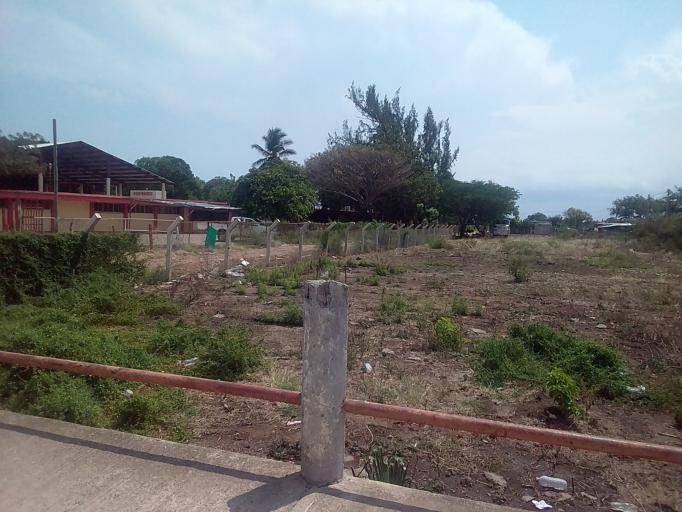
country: MX
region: Oaxaca
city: Union Hidalgo
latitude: 16.4566
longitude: -94.8293
